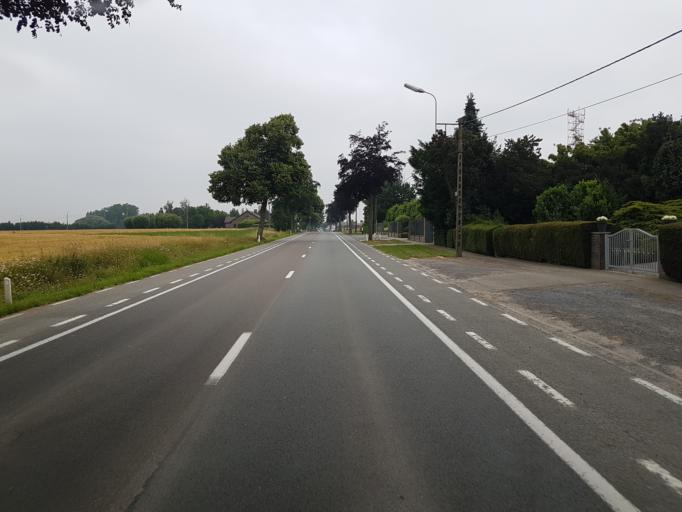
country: BE
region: Flanders
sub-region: Provincie Oost-Vlaanderen
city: Haaltert
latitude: 50.8762
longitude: 3.9704
